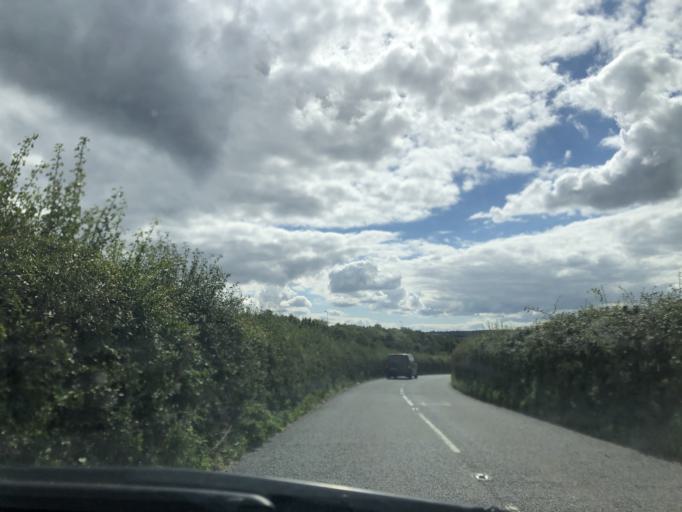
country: GB
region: England
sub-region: Kent
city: Halstead
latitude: 51.2996
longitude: 0.1439
